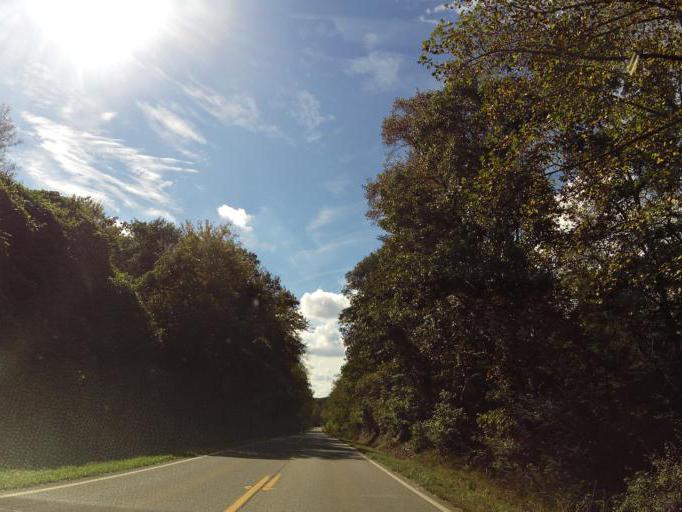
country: US
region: Georgia
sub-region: Pickens County
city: Nelson
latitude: 34.4121
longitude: -84.3931
